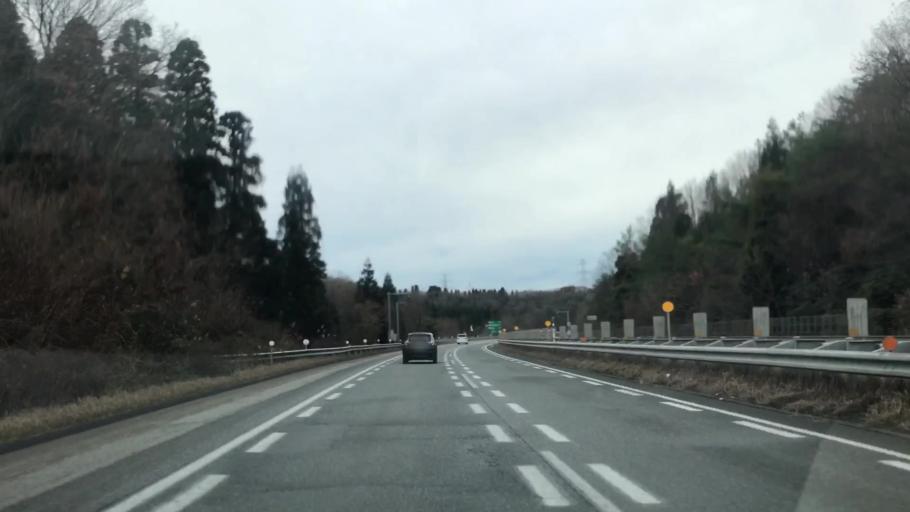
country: JP
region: Toyama
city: Kuragaki-kosugi
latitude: 36.6857
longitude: 137.1009
